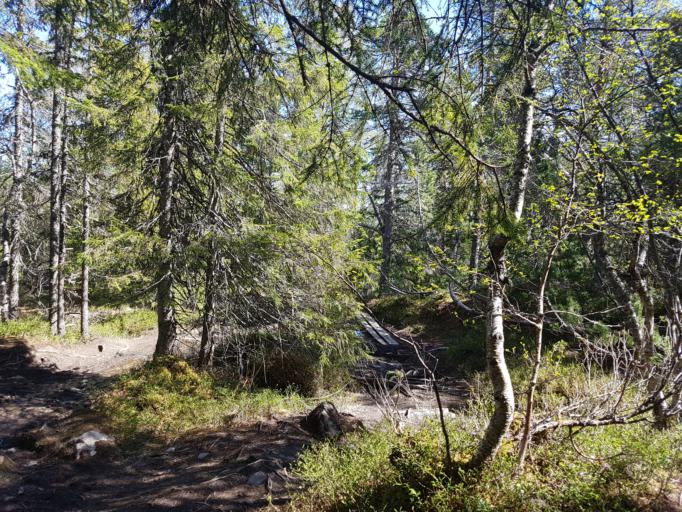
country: NO
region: Sor-Trondelag
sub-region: Trondheim
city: Trondheim
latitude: 63.4288
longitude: 10.3126
